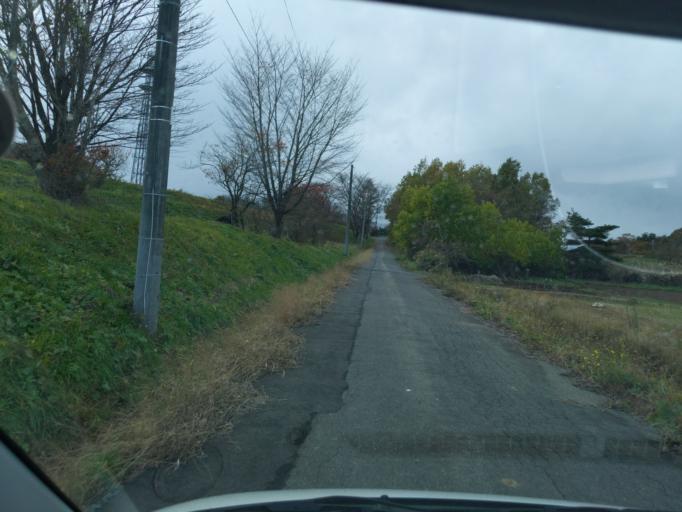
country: JP
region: Iwate
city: Mizusawa
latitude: 39.0453
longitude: 141.0739
